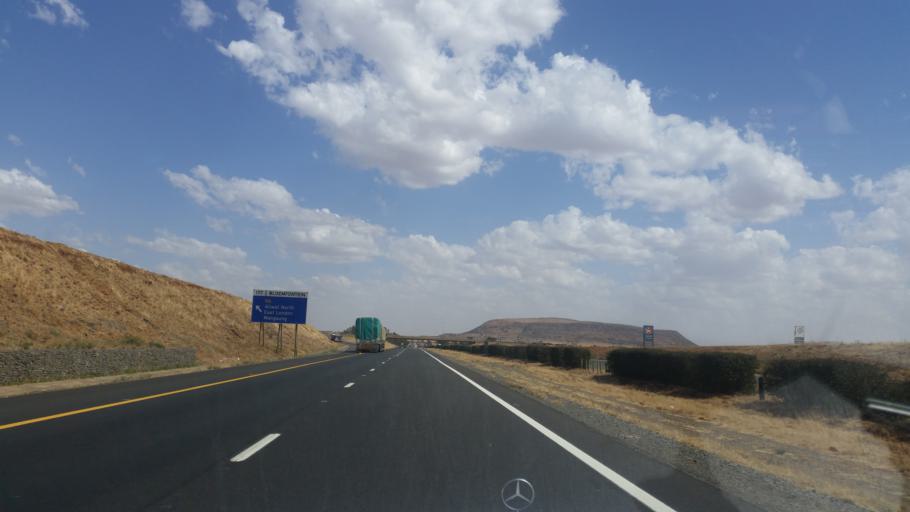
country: ZA
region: Orange Free State
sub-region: Mangaung Metropolitan Municipality
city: Bloemfontein
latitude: -29.1966
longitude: 26.1924
